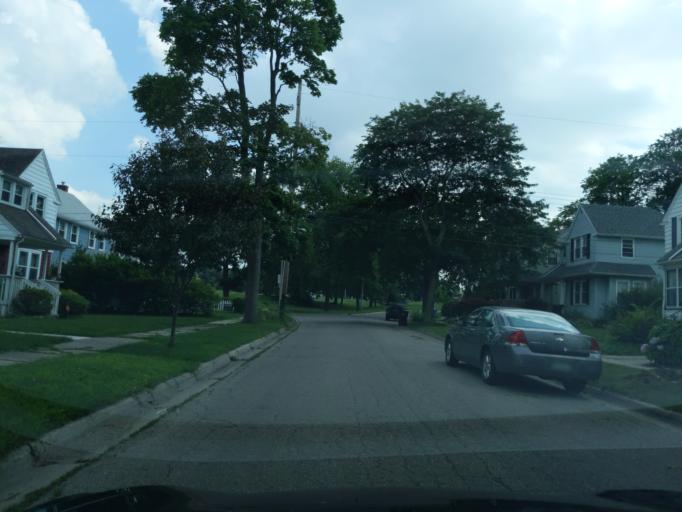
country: US
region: Michigan
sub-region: Ingham County
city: Lansing
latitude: 42.7175
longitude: -84.5736
